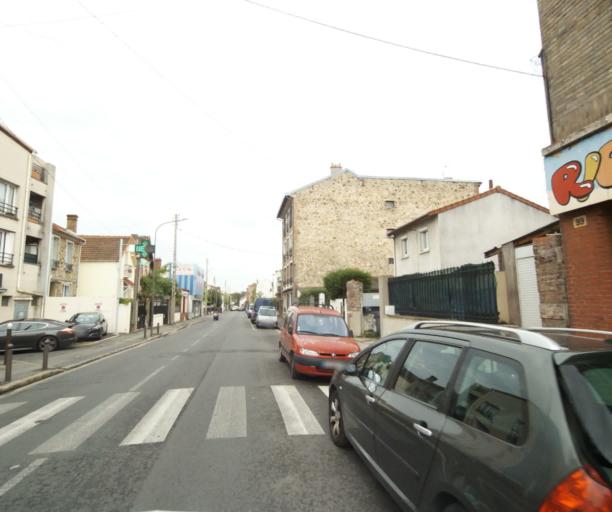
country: FR
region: Ile-de-France
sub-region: Departement du Val-d'Oise
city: Argenteuil
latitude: 48.9514
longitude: 2.2438
